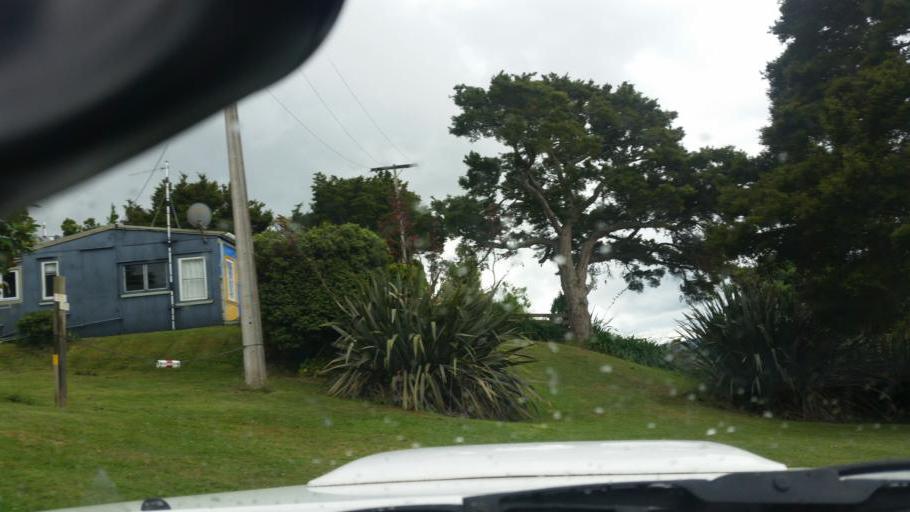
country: NZ
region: Auckland
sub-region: Auckland
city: Wellsford
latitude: -36.1544
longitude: 174.2279
